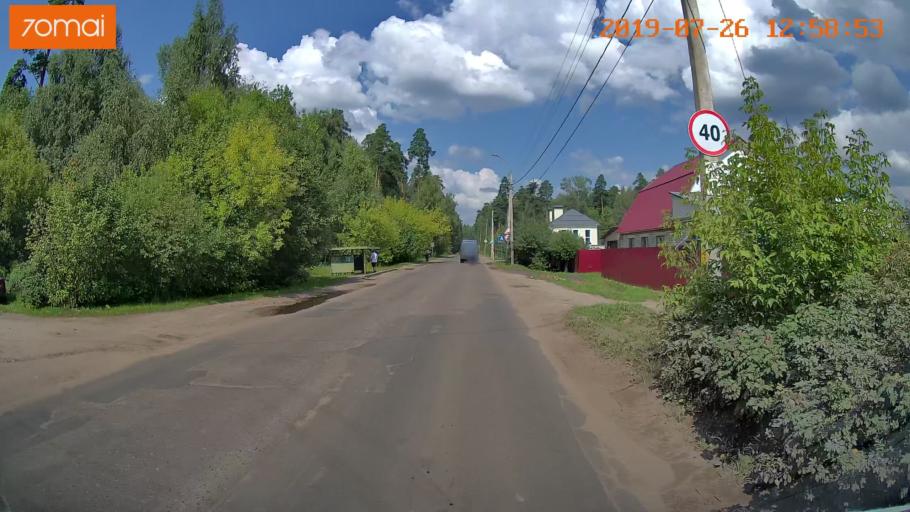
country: RU
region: Ivanovo
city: Bogorodskoye
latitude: 57.0260
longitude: 41.0208
